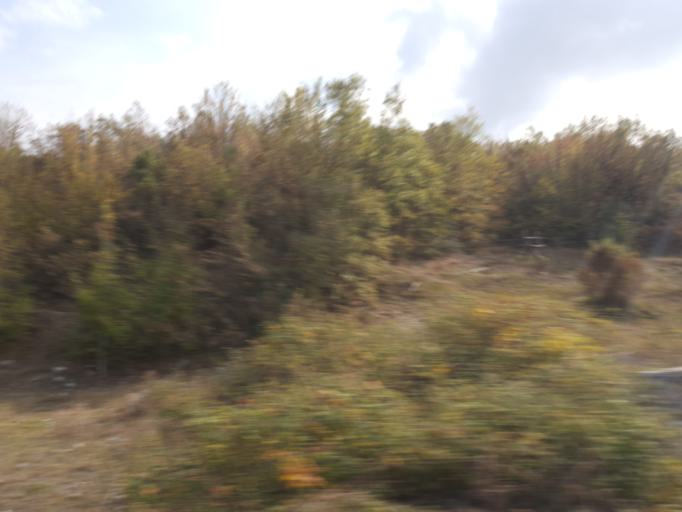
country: TR
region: Sinop
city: Sarayduzu
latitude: 41.3750
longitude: 34.9036
